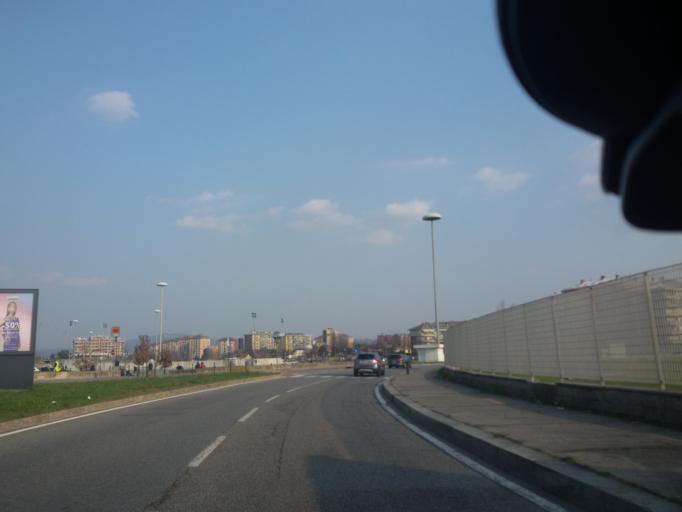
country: IT
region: Piedmont
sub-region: Provincia di Torino
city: Venaria Reale
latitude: 45.1083
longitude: 7.6370
